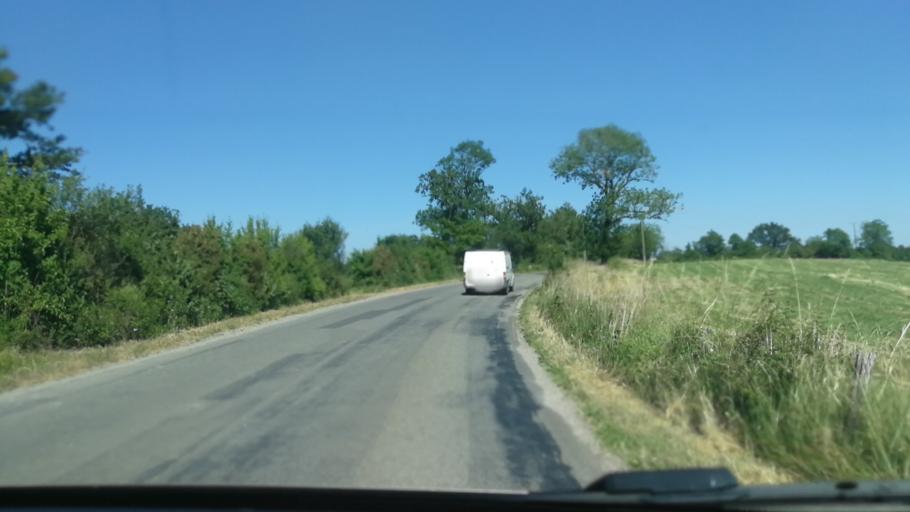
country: FR
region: Midi-Pyrenees
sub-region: Departement de l'Aveyron
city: Sebazac-Concoures
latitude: 44.4114
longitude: 2.5852
